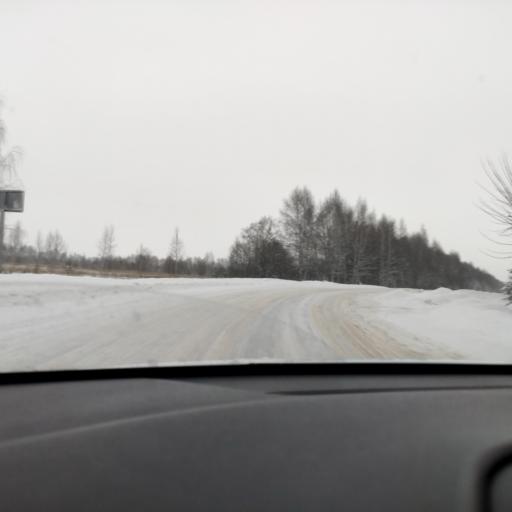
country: RU
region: Tatarstan
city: Vysokaya Gora
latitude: 55.9582
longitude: 49.1580
